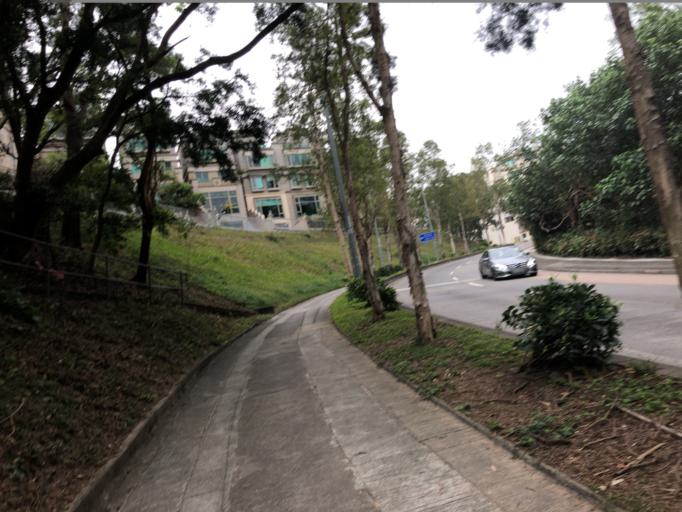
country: HK
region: Tai Po
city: Tai Po
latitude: 22.4649
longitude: 114.1930
